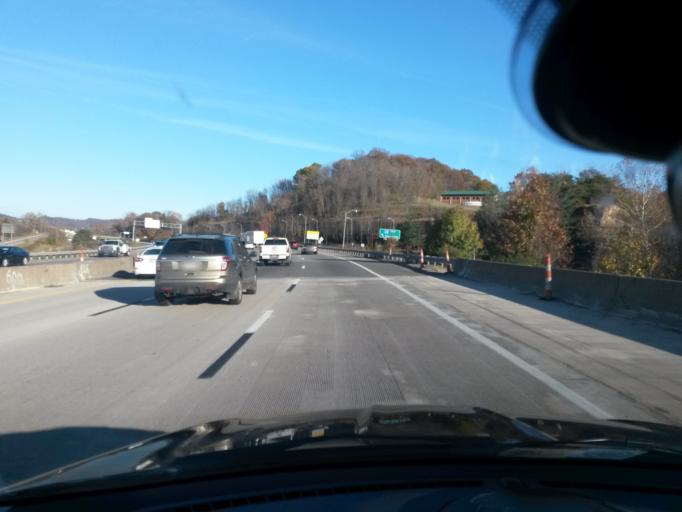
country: US
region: West Virginia
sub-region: Kanawha County
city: South Charleston
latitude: 38.3583
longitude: -81.7027
